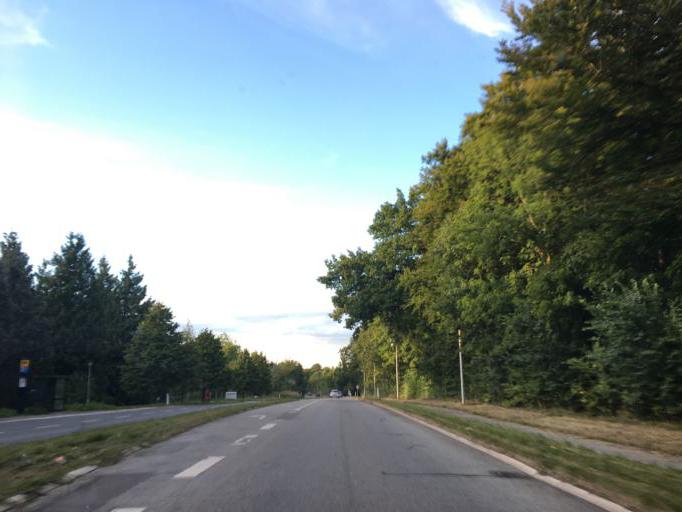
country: DK
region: Capital Region
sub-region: Horsholm Kommune
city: Horsholm
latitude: 55.8728
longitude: 12.4976
